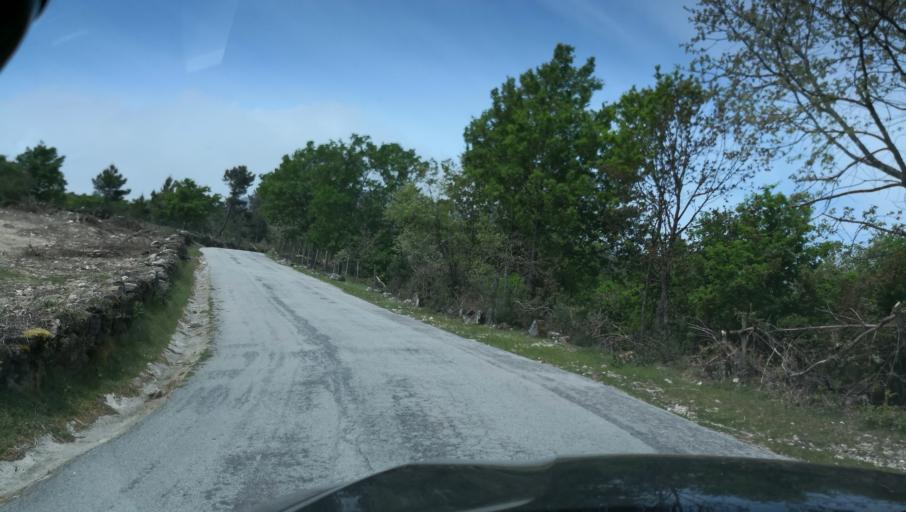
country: PT
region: Vila Real
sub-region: Vila Real
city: Vila Real
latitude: 41.2903
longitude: -7.8056
